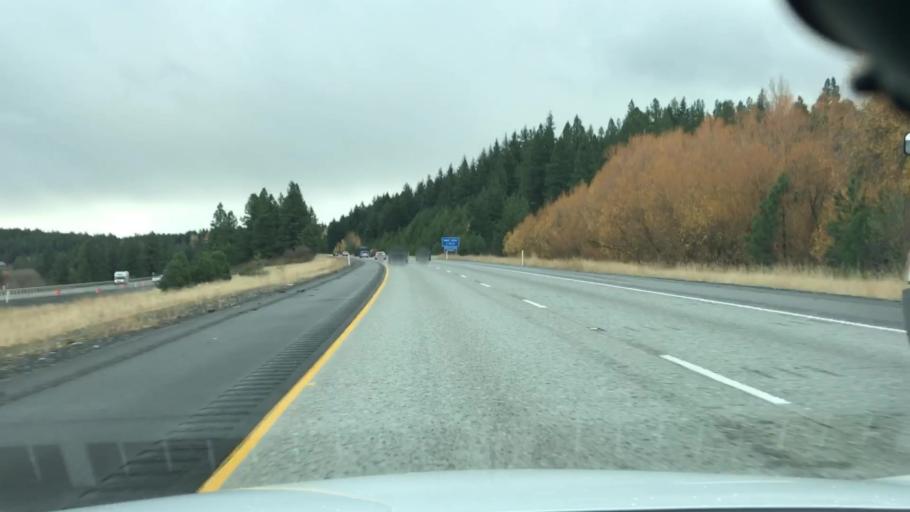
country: US
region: Washington
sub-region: Kittitas County
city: Cle Elum
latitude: 47.1645
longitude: -120.8743
